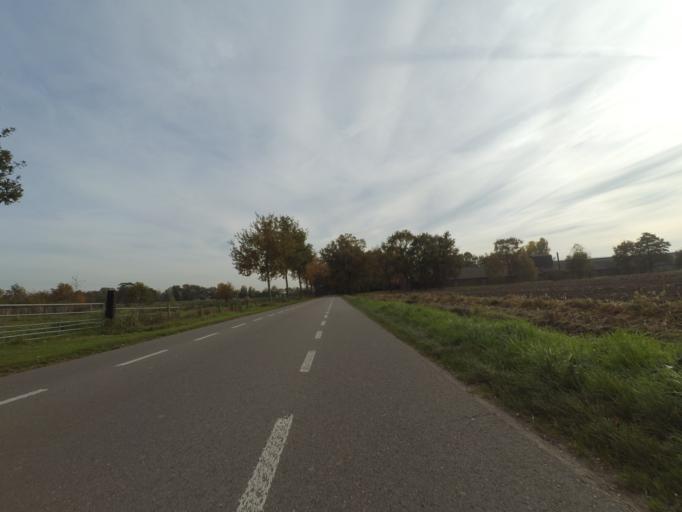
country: NL
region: Gelderland
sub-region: Gemeente Barneveld
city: Barneveld
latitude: 52.1163
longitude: 5.5499
